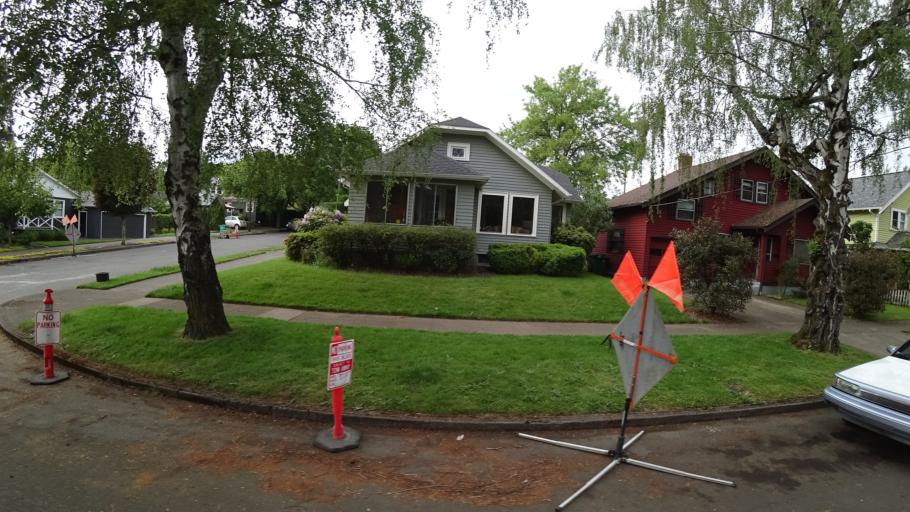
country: US
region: Oregon
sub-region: Multnomah County
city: Portland
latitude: 45.5186
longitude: -122.6194
